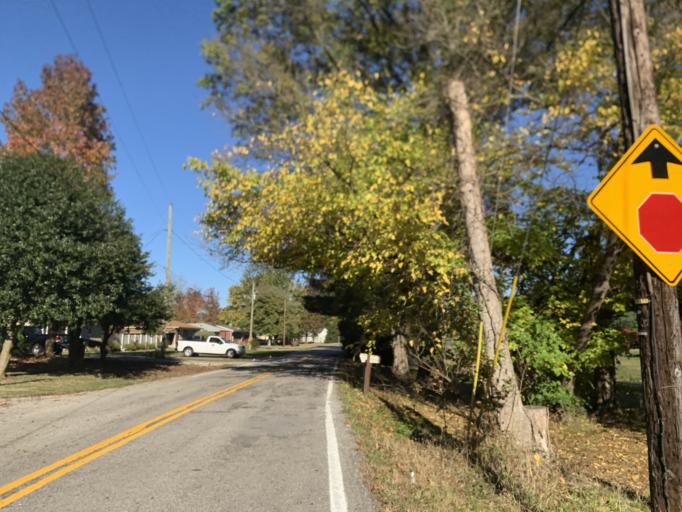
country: US
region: Kentucky
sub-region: Jefferson County
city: Pleasure Ridge Park
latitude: 38.1560
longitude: -85.8695
